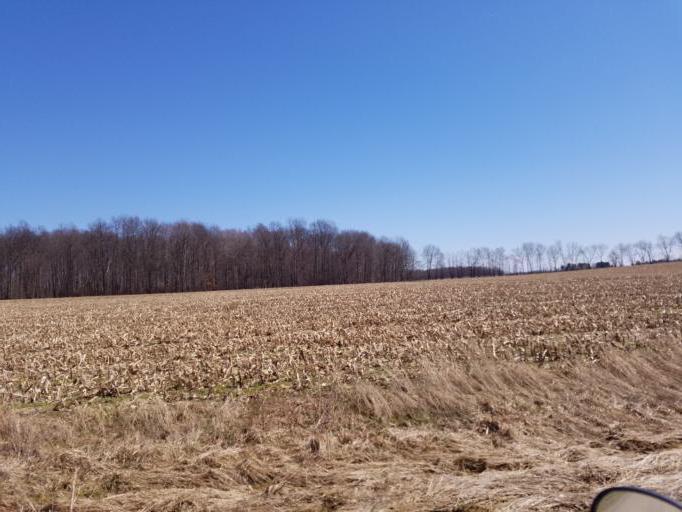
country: US
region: Ohio
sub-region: Knox County
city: Fredericktown
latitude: 40.5402
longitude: -82.5245
